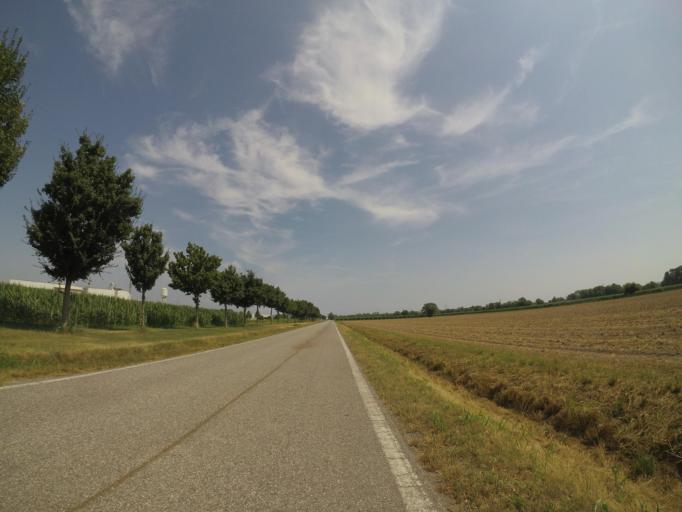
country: IT
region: Friuli Venezia Giulia
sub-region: Provincia di Pordenone
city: Rosa
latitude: 45.9344
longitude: 12.8891
